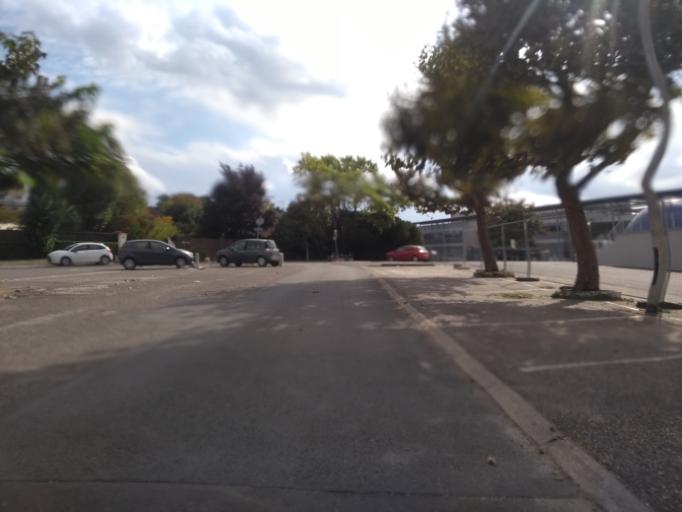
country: FR
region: Aquitaine
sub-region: Departement de la Gironde
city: Talence
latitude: 44.8235
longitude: -0.6067
